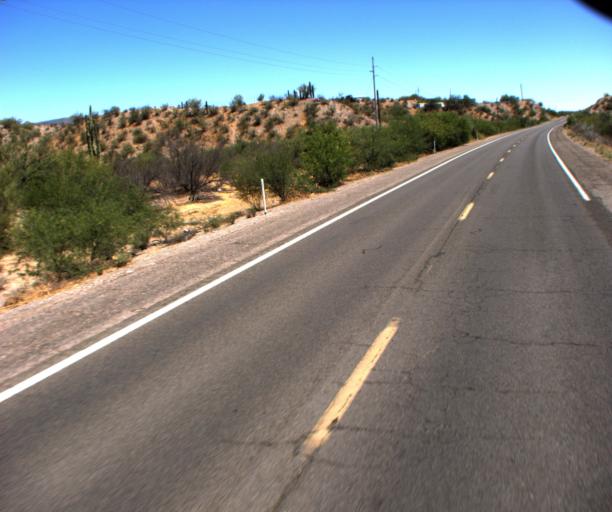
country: US
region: Arizona
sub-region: Pinal County
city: Kearny
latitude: 32.9627
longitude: -110.7520
